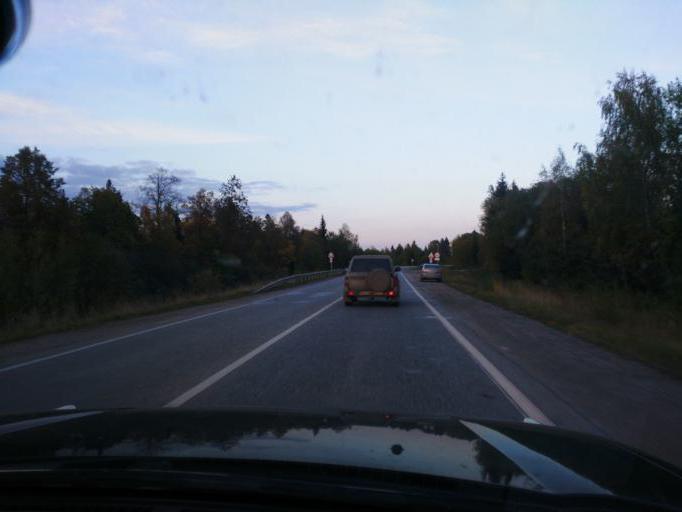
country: RU
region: Perm
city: Polazna
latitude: 58.3036
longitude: 56.6196
